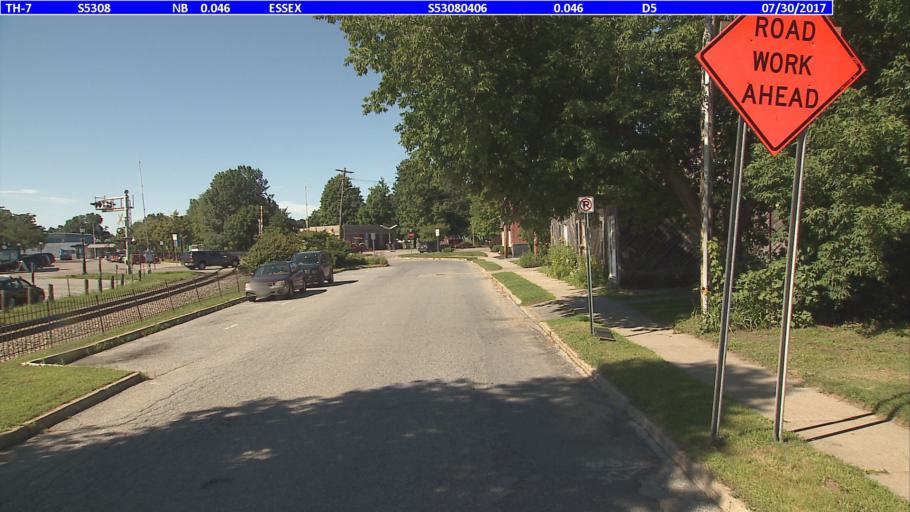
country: US
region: Vermont
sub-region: Chittenden County
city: Essex Junction
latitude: 44.4907
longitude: -73.1095
